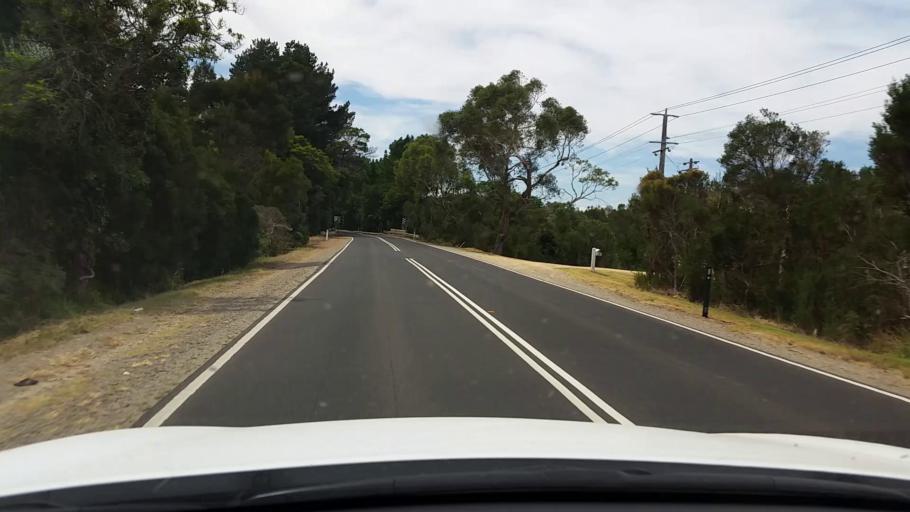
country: AU
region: Victoria
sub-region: Mornington Peninsula
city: Mount Martha
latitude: -38.2806
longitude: 145.0701
